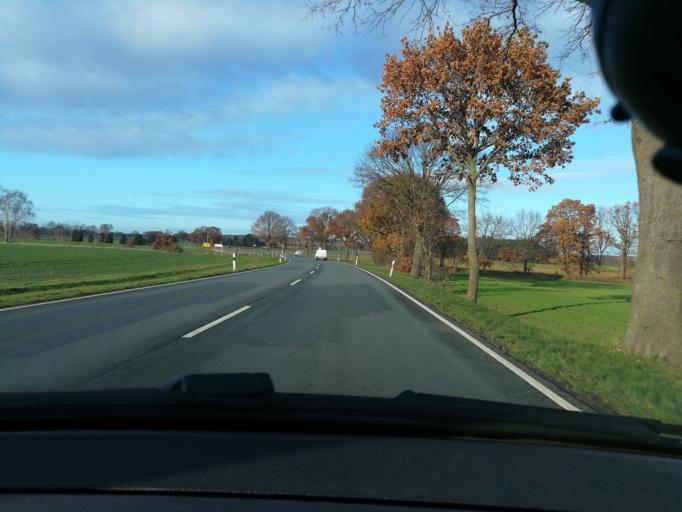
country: DE
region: Lower Saxony
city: Uchte
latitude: 52.5149
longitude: 8.9007
